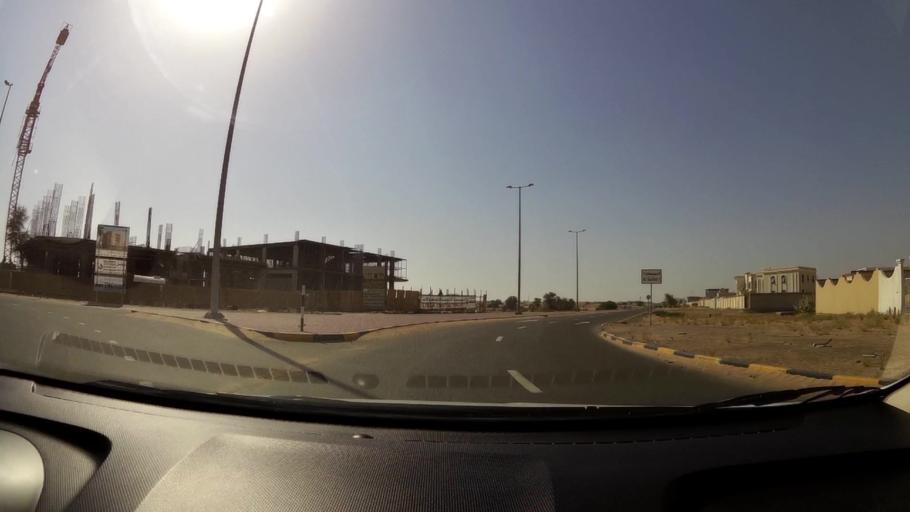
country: AE
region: Umm al Qaywayn
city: Umm al Qaywayn
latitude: 25.4737
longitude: 55.5964
